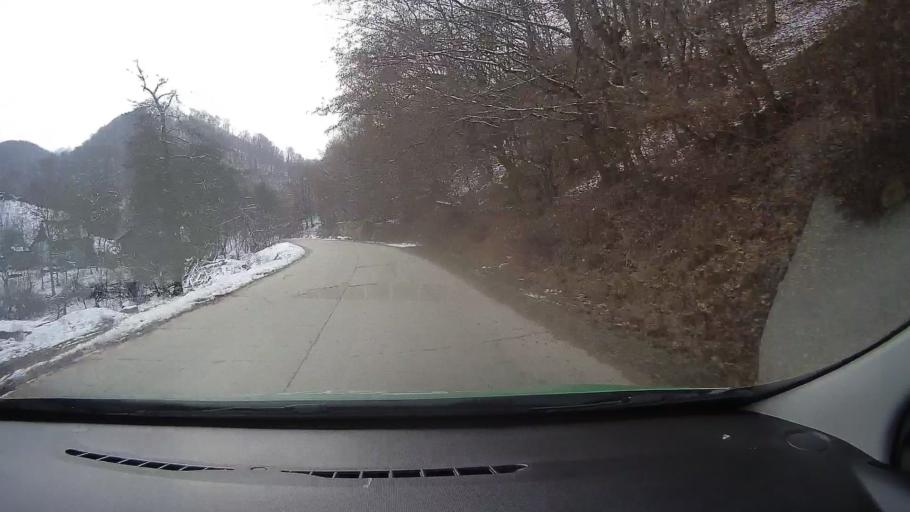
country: RO
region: Alba
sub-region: Oras Zlatna
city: Zlatna
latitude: 46.1091
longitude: 23.1965
